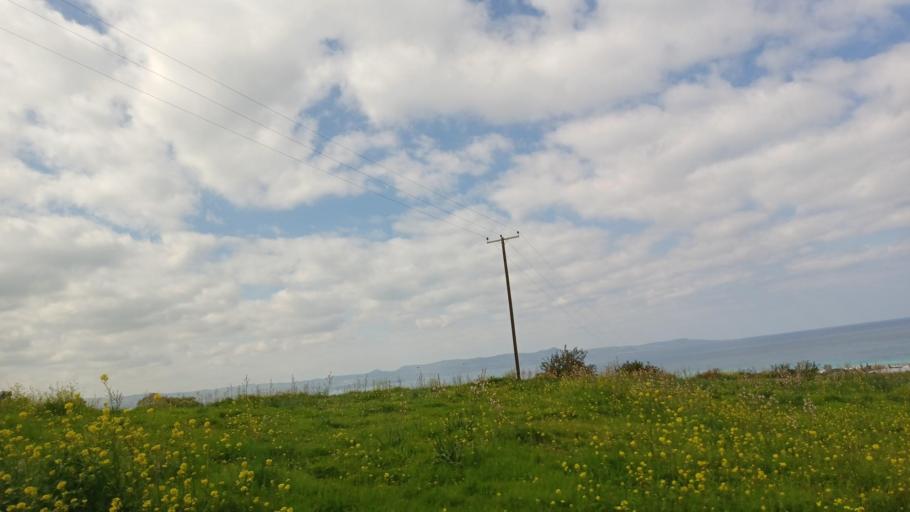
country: CY
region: Pafos
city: Polis
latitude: 35.1022
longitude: 32.5146
